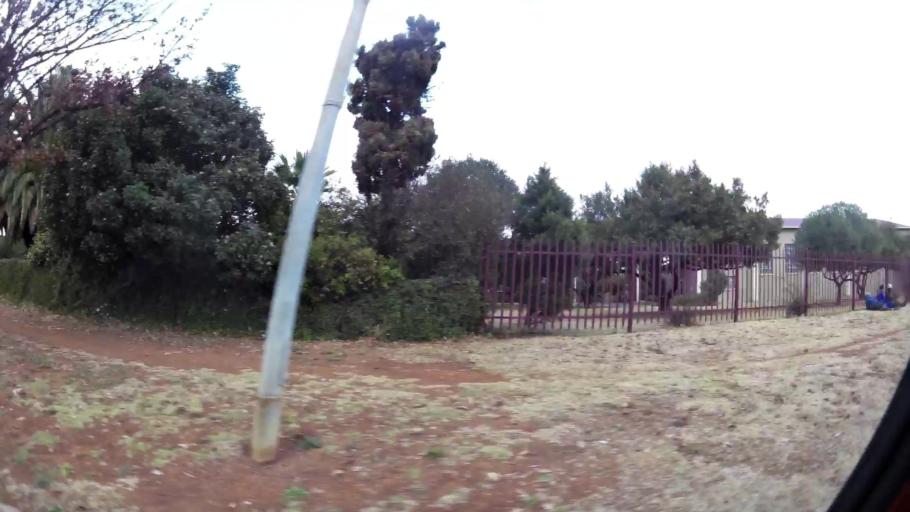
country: ZA
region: Gauteng
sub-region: Sedibeng District Municipality
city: Vanderbijlpark
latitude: -26.7184
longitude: 27.8516
